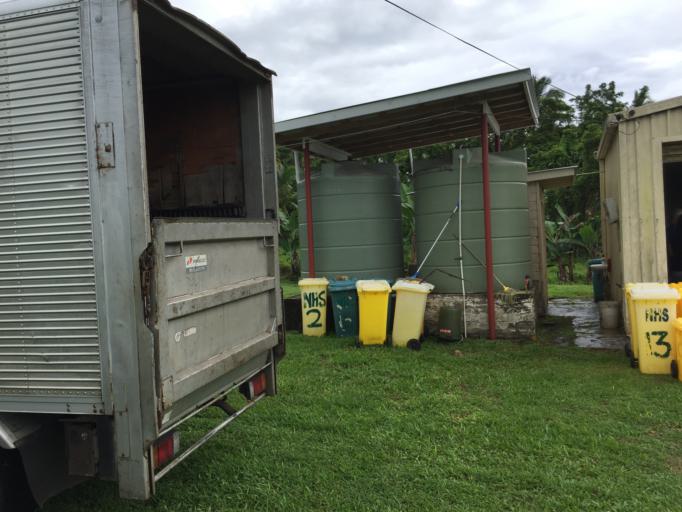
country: WS
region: Fa`asaleleaga
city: Safotulafai
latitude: -13.6583
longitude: -172.2470
